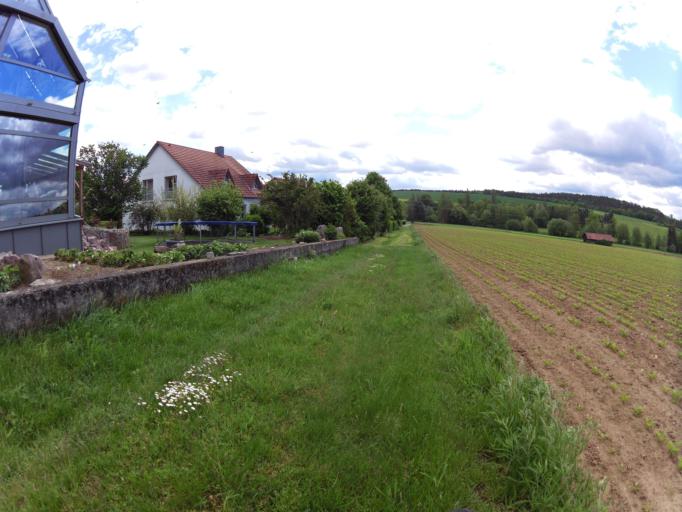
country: DE
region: Bavaria
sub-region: Regierungsbezirk Unterfranken
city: Volkach
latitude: 49.8742
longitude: 10.2510
